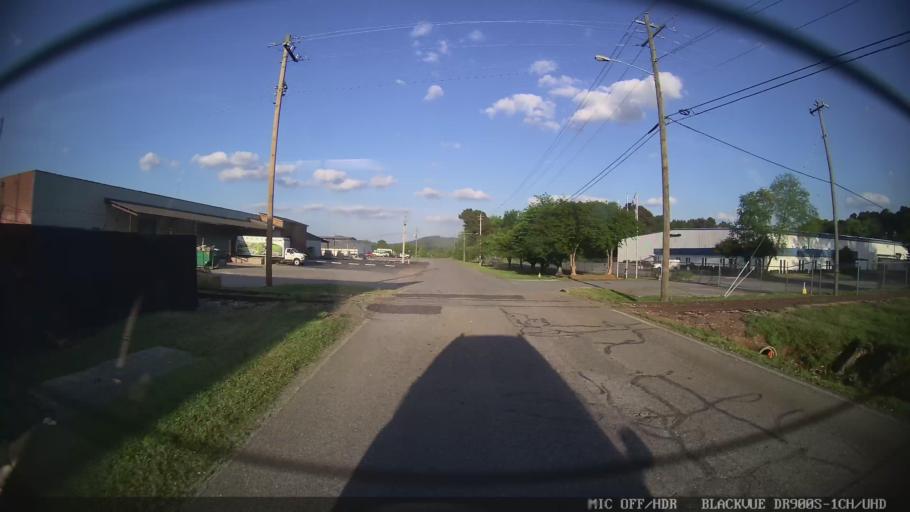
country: US
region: Georgia
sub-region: Bartow County
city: Cartersville
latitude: 34.1458
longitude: -84.7957
